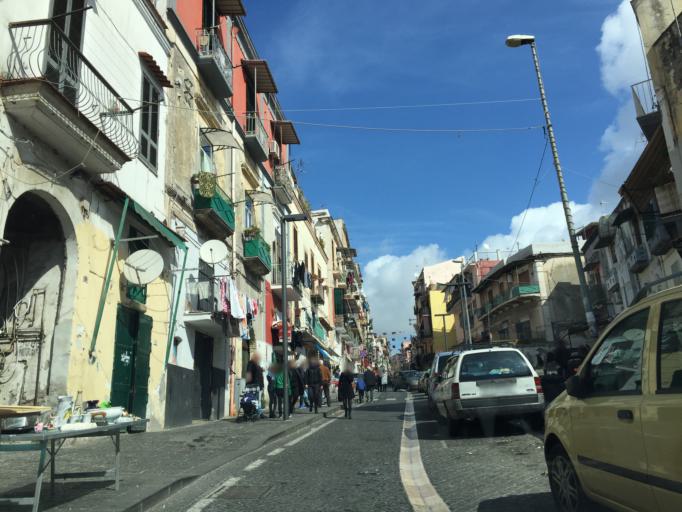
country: IT
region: Campania
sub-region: Provincia di Napoli
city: Portici
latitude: 40.8088
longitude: 14.3490
